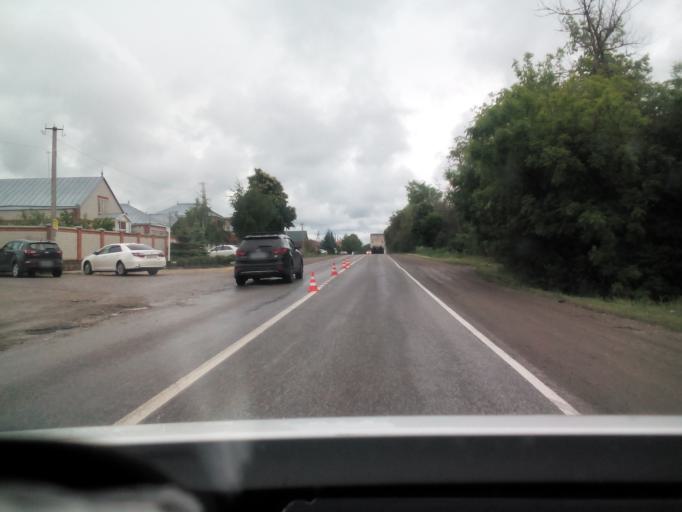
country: RU
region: Stavropol'skiy
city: Yessentuki
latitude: 44.0710
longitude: 42.8402
